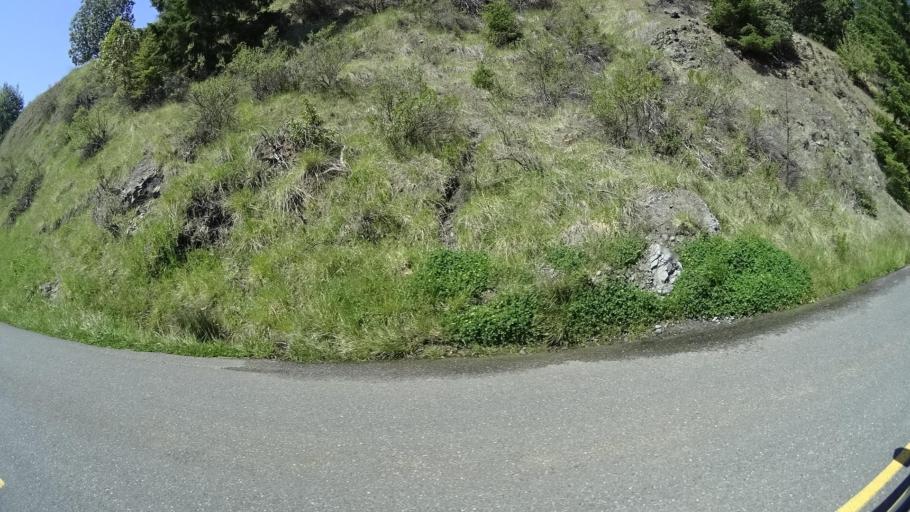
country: US
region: California
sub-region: Humboldt County
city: Redway
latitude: 40.1130
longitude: -123.6723
